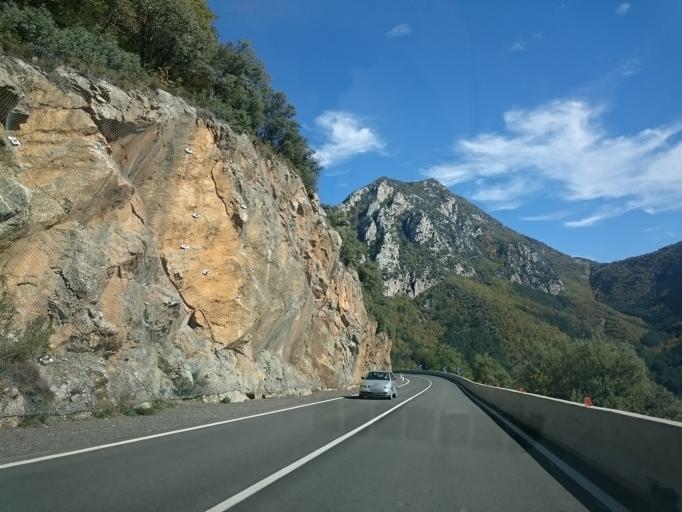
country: ES
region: Aragon
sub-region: Provincia de Huesca
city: Sopeira
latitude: 42.3677
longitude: 0.7369
